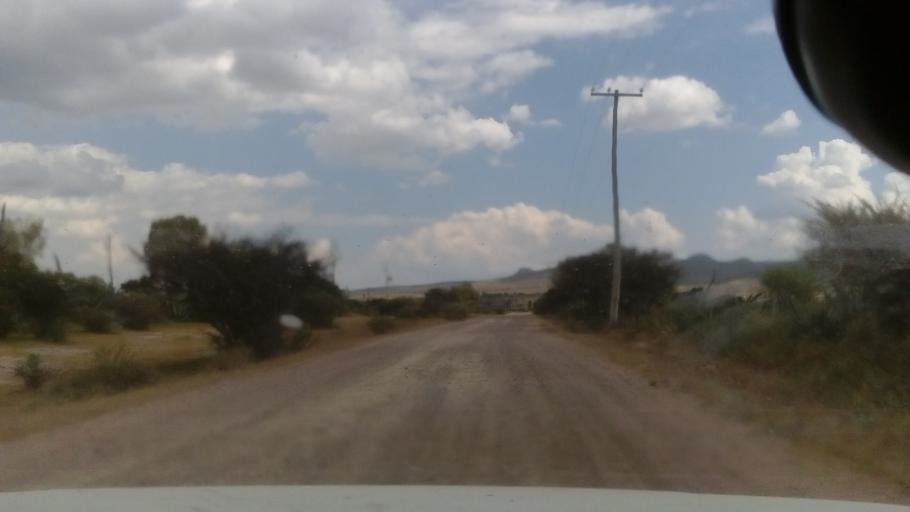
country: MX
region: Guanajuato
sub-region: Silao de la Victoria
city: San Francisco (Banos de Agua Caliente)
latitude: 21.2012
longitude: -101.4390
